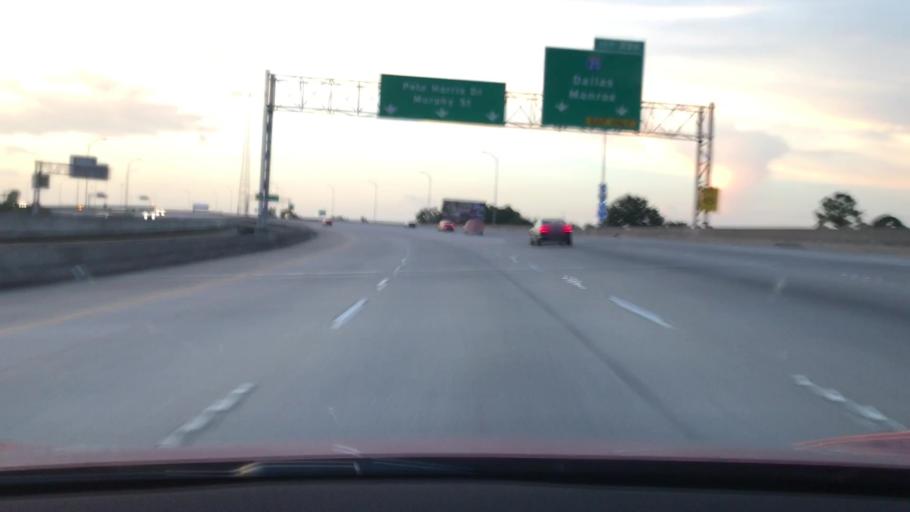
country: US
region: Louisiana
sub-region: Bossier Parish
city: Bossier City
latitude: 32.4896
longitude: -93.7550
